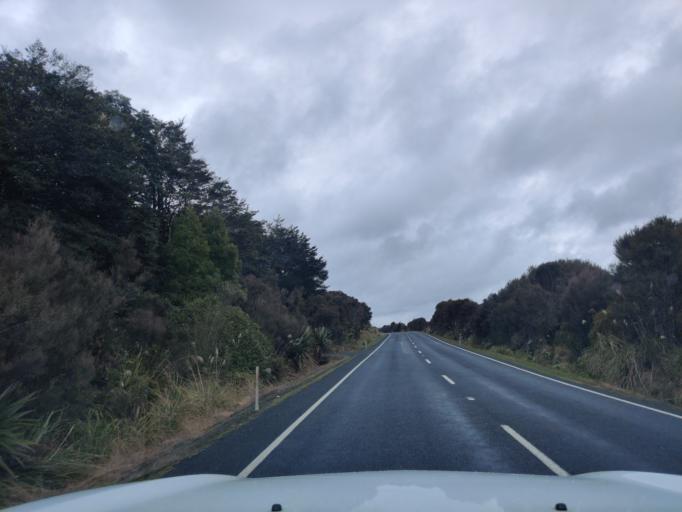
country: NZ
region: Manawatu-Wanganui
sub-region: Ruapehu District
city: Waiouru
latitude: -39.3344
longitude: 175.3803
